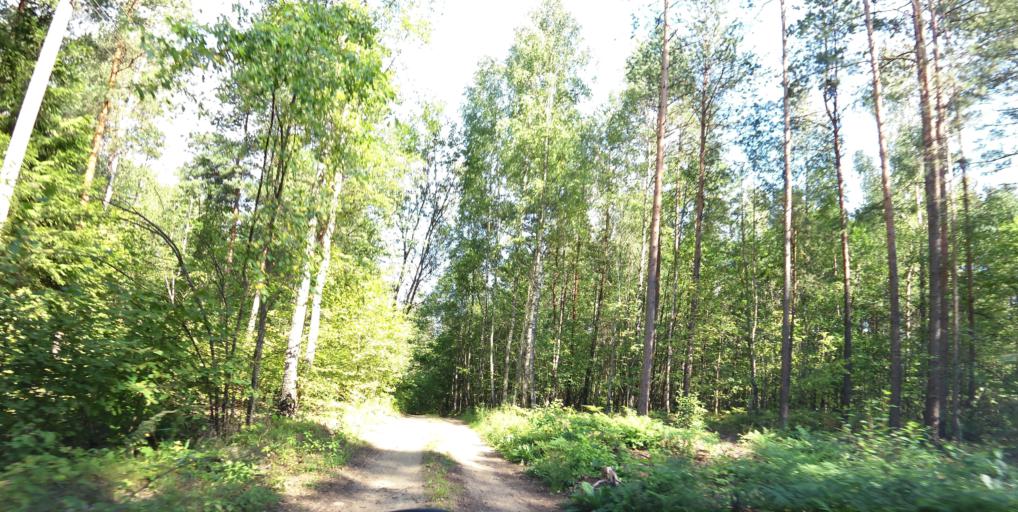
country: LT
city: Grigiskes
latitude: 54.7453
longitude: 25.0232
